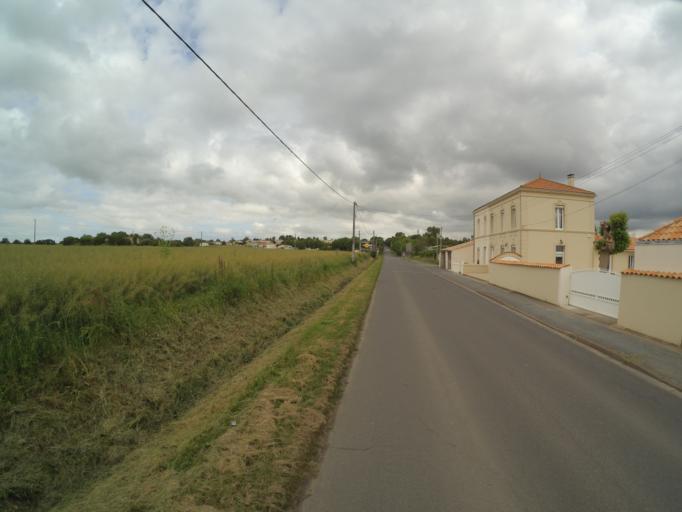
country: FR
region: Poitou-Charentes
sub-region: Departement de la Charente-Maritime
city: Breuil-Magne
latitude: 45.9601
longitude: -0.9696
